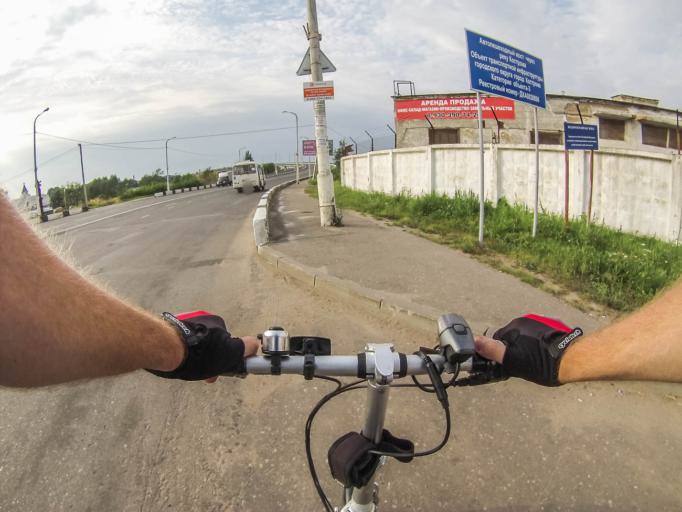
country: RU
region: Kostroma
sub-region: Kostromskoy Rayon
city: Kostroma
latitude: 57.7762
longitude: 40.9046
